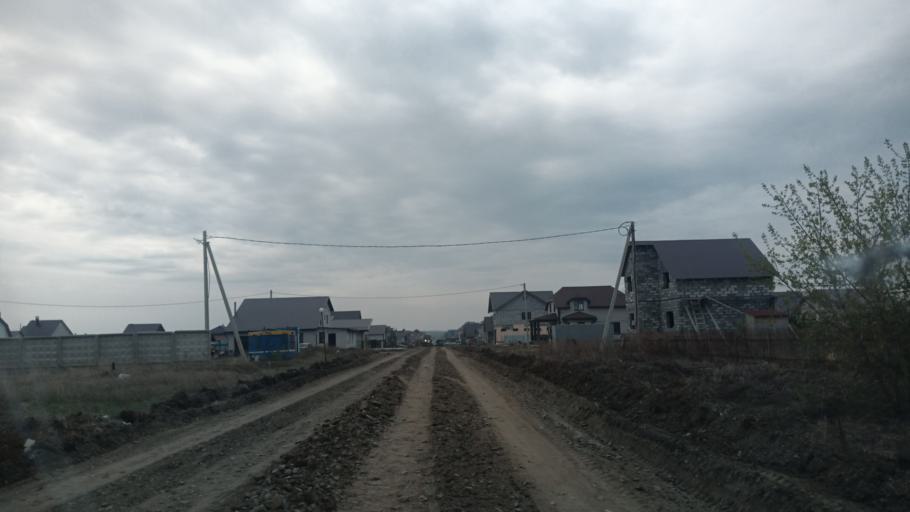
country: RU
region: Altai Krai
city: Yuzhnyy
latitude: 53.2285
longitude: 83.6914
